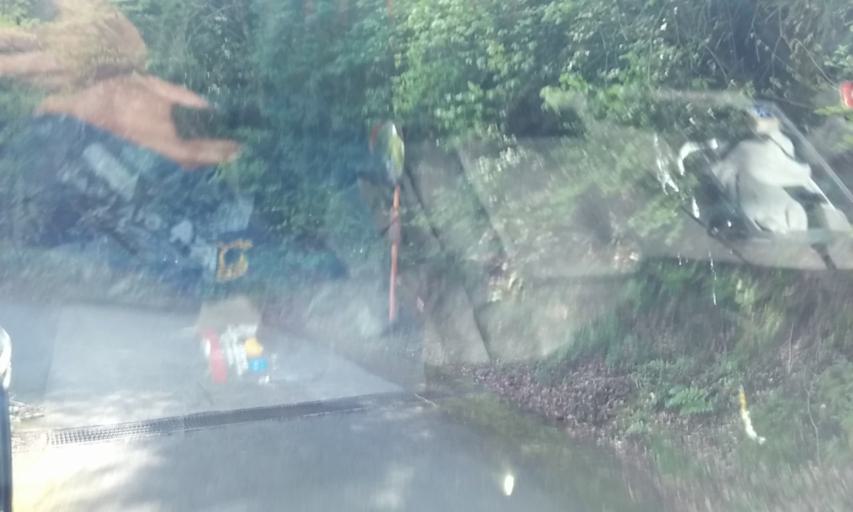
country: JP
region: Ehime
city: Niihama
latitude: 33.8742
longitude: 133.3039
